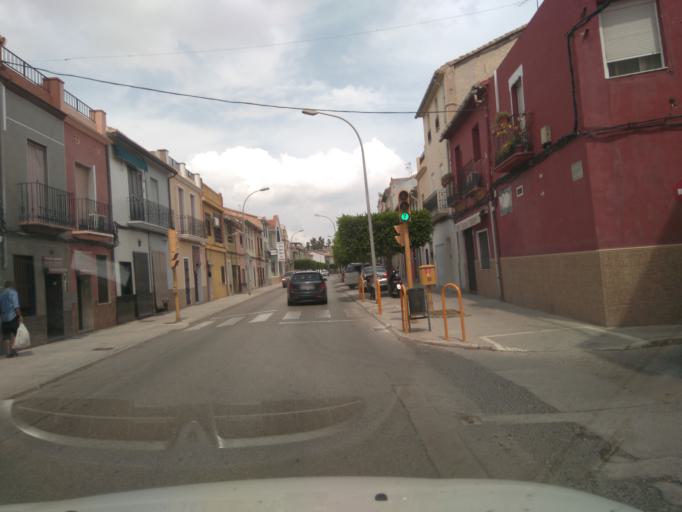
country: ES
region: Valencia
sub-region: Provincia de Valencia
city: Carcaixent
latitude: 39.1270
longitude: -0.4496
